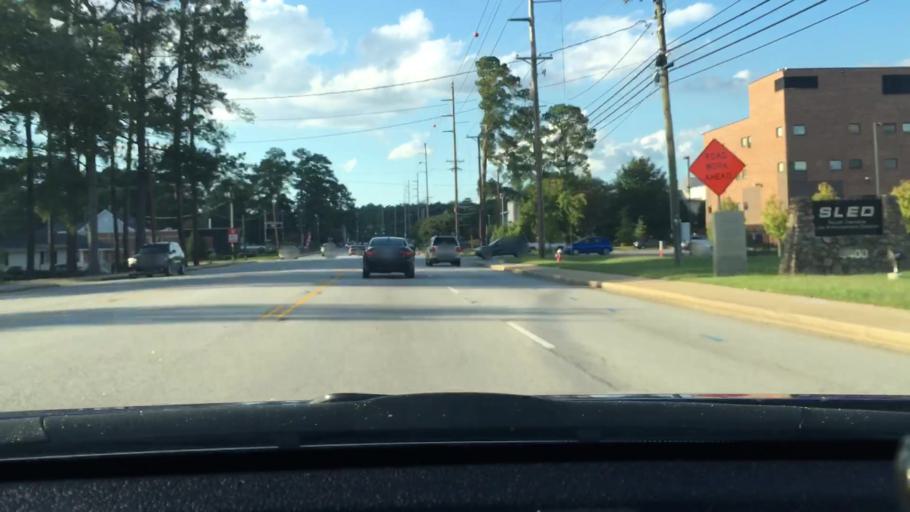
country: US
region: South Carolina
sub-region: Lexington County
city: Saint Andrews
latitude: 34.0658
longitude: -81.1166
